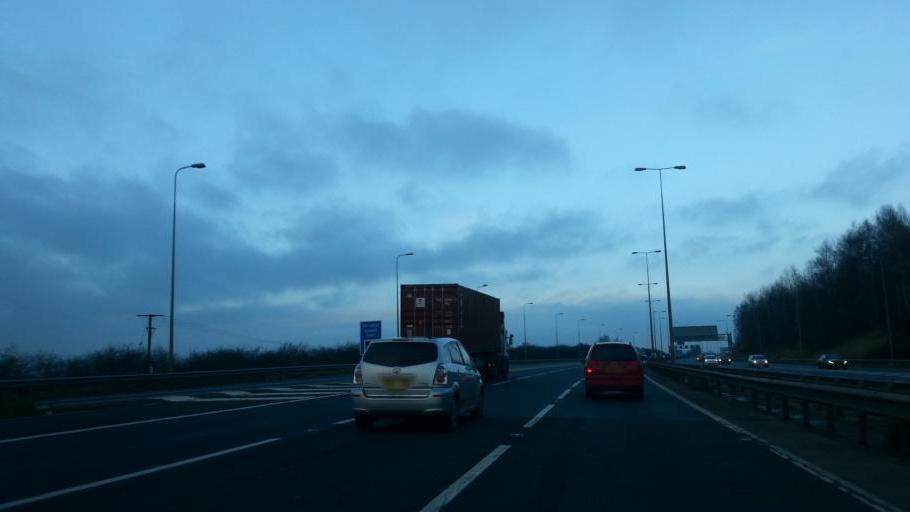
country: GB
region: England
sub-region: Worcestershire
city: Fernhill Heath
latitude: 52.2158
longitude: -2.1559
